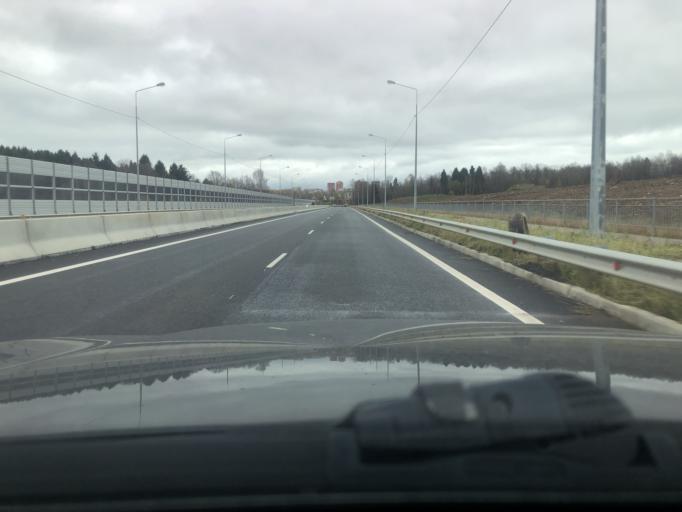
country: RU
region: Moskovskaya
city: Sergiyev Posad
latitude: 56.3373
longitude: 38.1047
